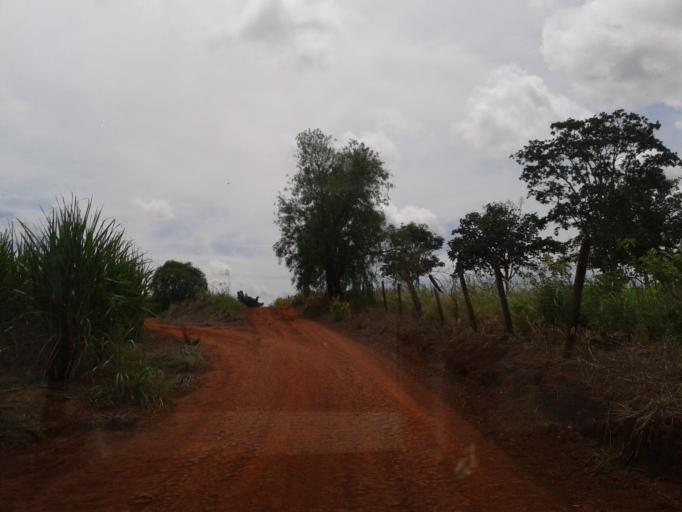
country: BR
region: Minas Gerais
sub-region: Centralina
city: Centralina
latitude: -18.5881
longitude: -49.2691
